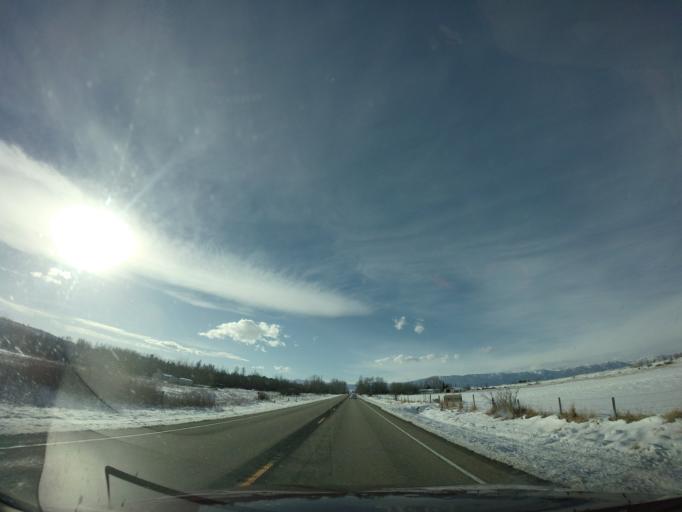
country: US
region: Montana
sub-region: Carbon County
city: Red Lodge
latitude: 45.3274
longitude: -109.1875
